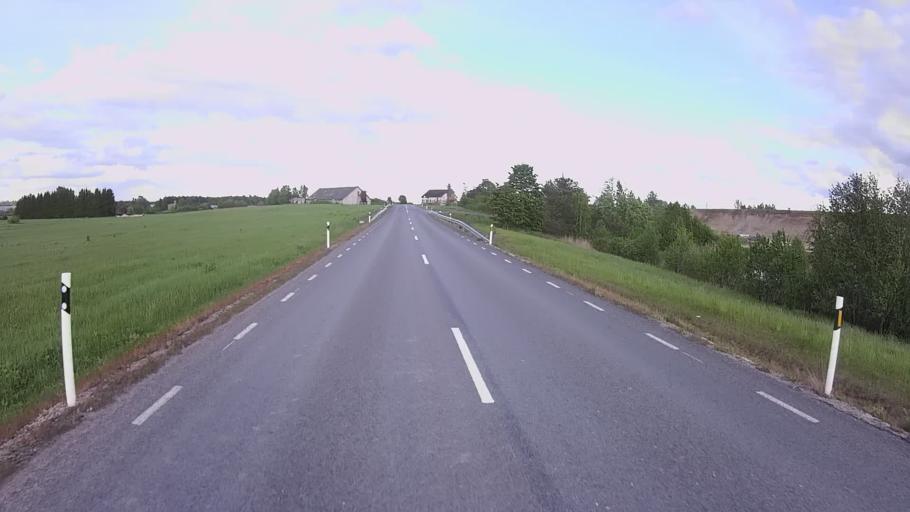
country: EE
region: Jogevamaa
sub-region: Mustvee linn
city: Mustvee
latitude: 59.0391
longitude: 27.0711
